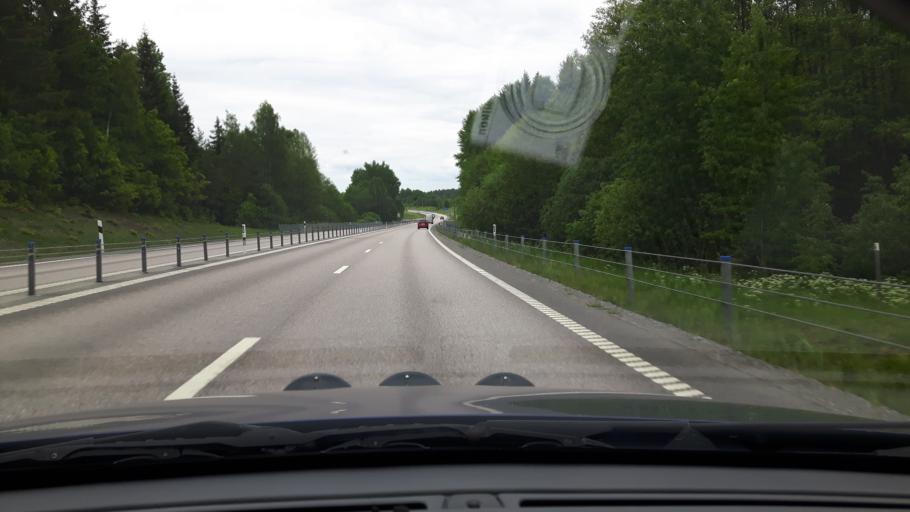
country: SE
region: Soedermanland
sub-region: Flens Kommun
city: Flen
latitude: 59.0378
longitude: 16.5548
